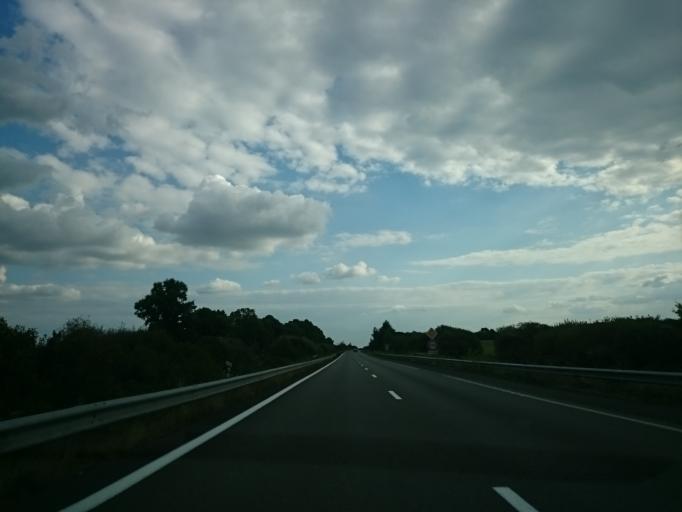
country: FR
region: Pays de la Loire
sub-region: Departement de la Loire-Atlantique
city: La Grigonnais
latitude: 47.5303
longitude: -1.6381
